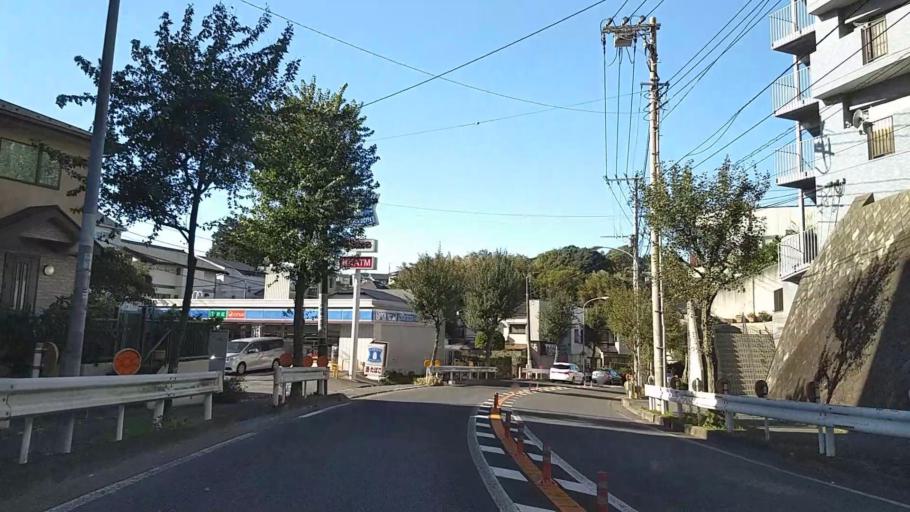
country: JP
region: Kanagawa
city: Yokohama
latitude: 35.4237
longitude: 139.5754
